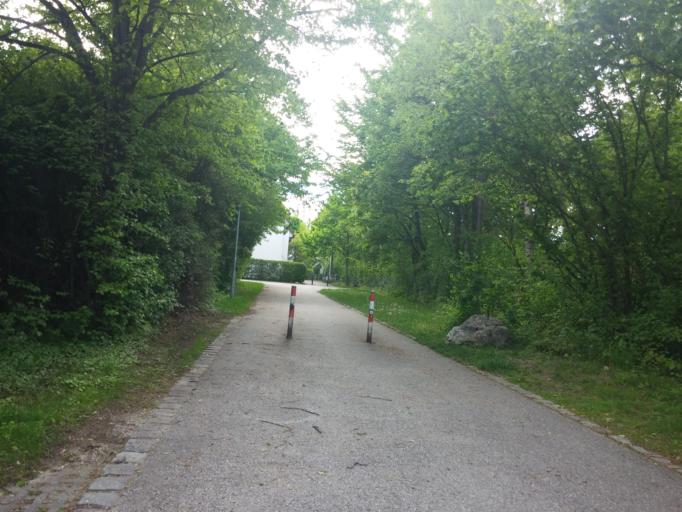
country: DE
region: Bavaria
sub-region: Upper Bavaria
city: Bogenhausen
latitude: 48.1462
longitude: 11.6437
